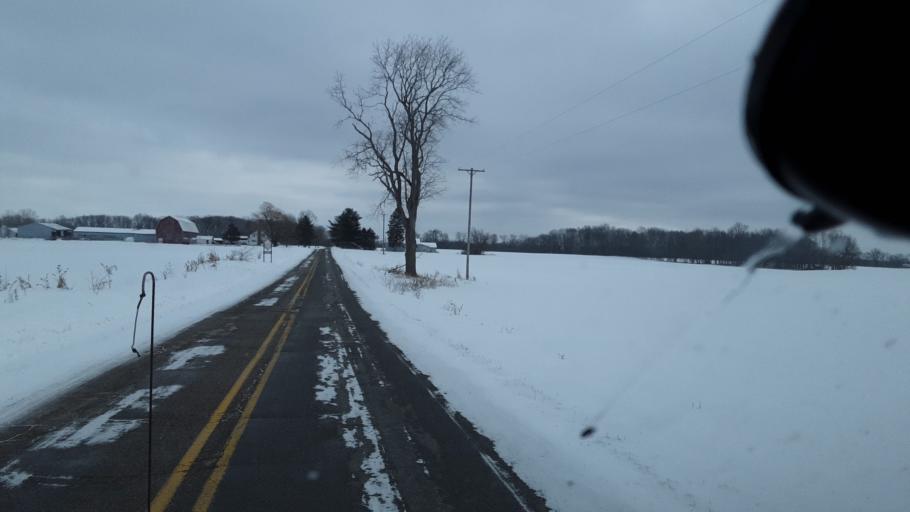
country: US
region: Michigan
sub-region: Ingham County
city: Mason
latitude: 42.5333
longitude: -84.4025
